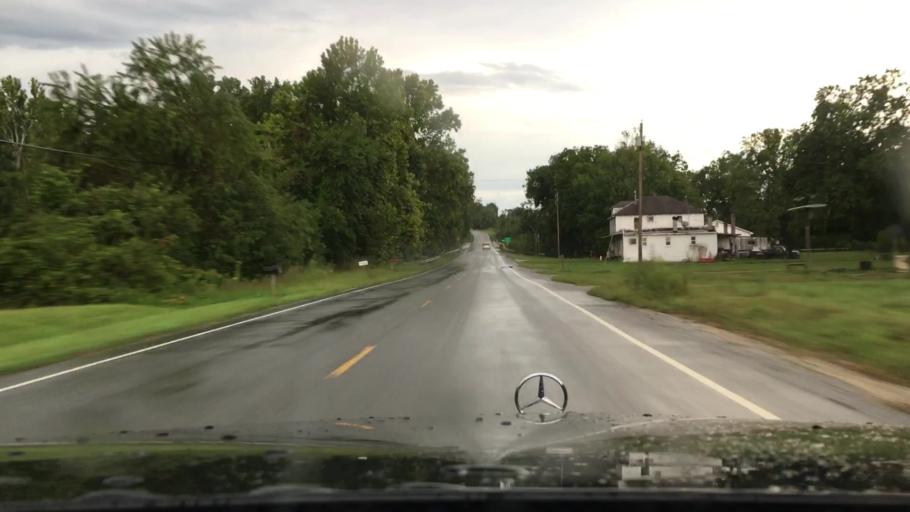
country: US
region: Virginia
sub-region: Amherst County
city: Amherst
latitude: 37.7041
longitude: -79.0261
